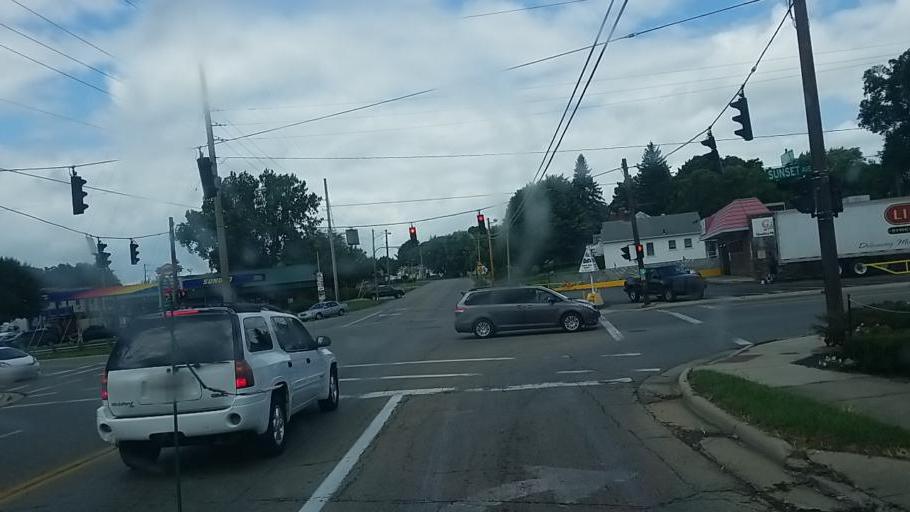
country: US
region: Ohio
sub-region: Clark County
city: Springfield
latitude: 39.9048
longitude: -83.7917
